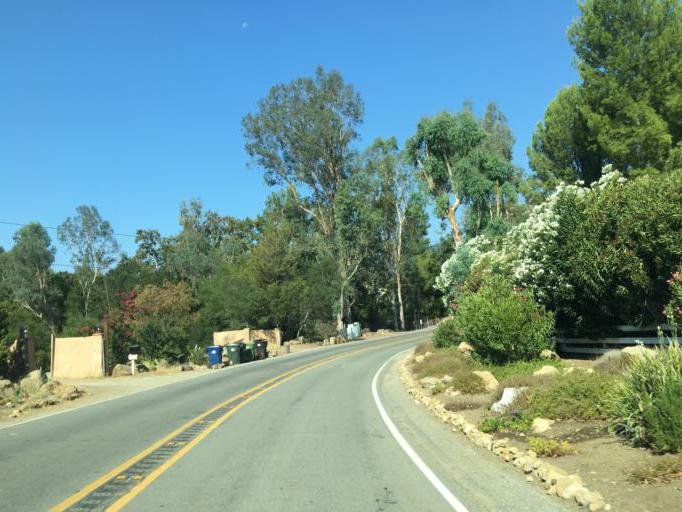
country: US
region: California
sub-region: Los Angeles County
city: Topanga
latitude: 34.1013
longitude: -118.6580
